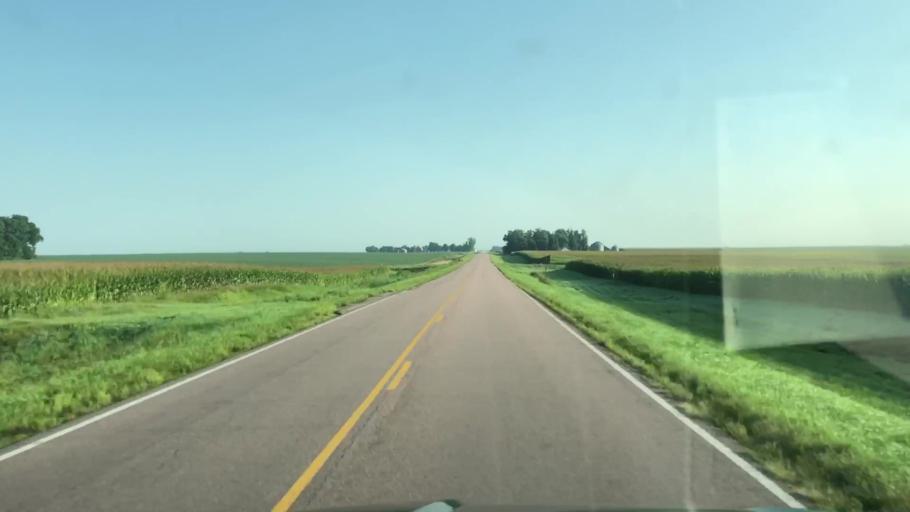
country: US
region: Iowa
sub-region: Lyon County
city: George
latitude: 43.3000
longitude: -95.9993
